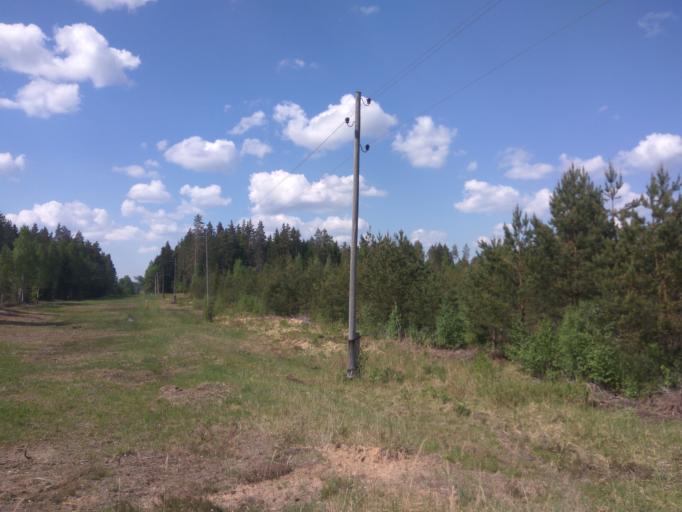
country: LV
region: Kuldigas Rajons
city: Kuldiga
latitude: 57.1852
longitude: 21.9933
